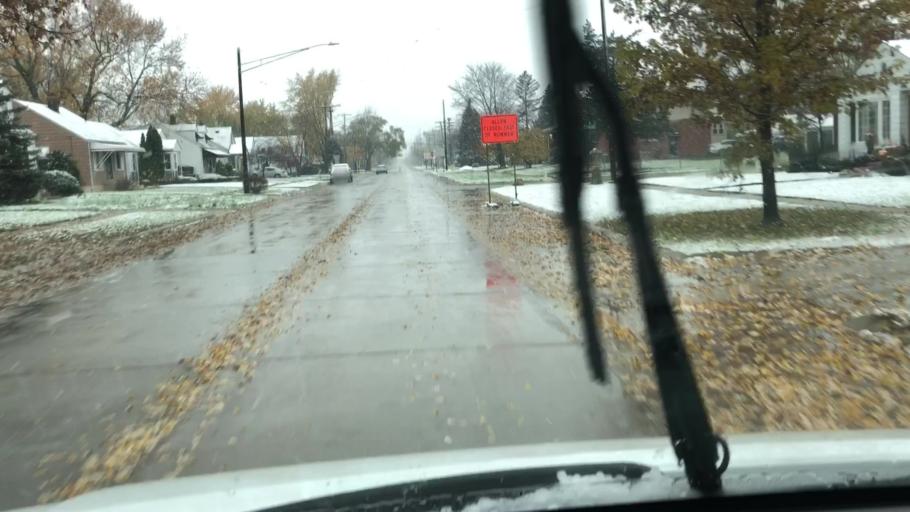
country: US
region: Michigan
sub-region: Macomb County
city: Eastpointe
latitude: 42.4572
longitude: -82.9692
